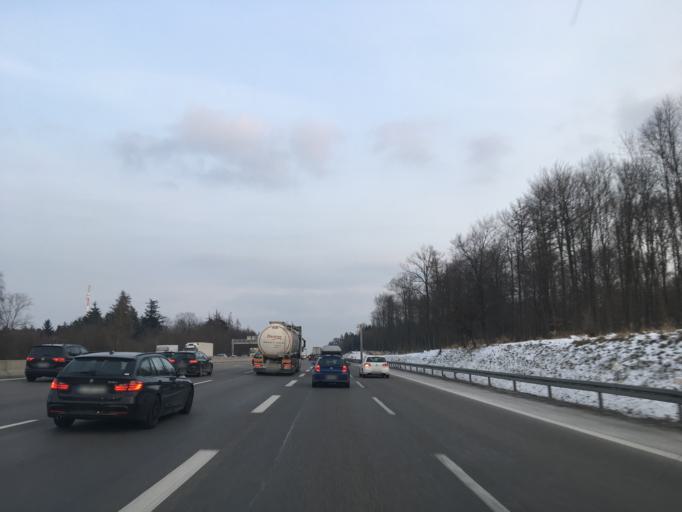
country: DE
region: Baden-Wuerttemberg
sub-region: Regierungsbezirk Stuttgart
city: Schonaich
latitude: 48.7206
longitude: 9.0781
